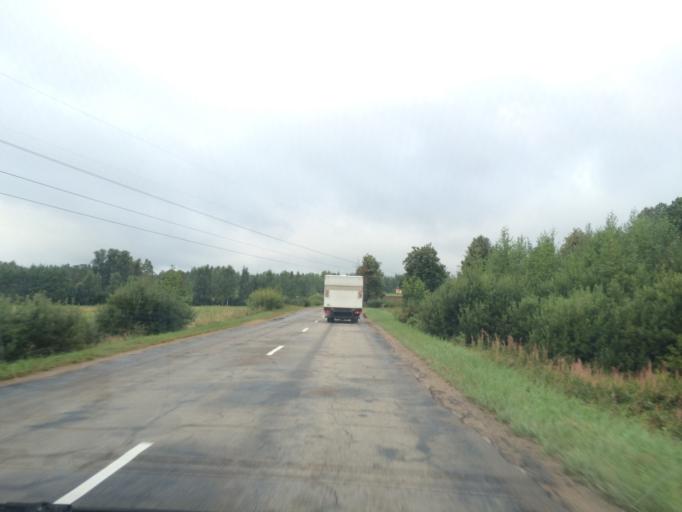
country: LV
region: Ikskile
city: Ikskile
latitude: 56.8592
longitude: 24.5475
